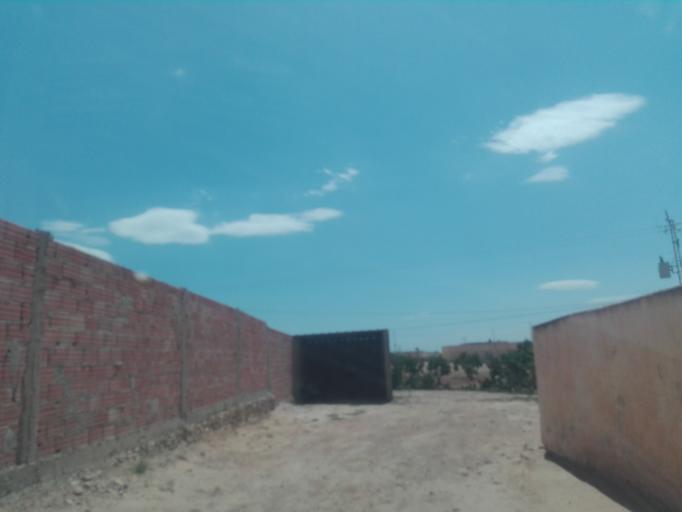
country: TN
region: Safaqis
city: Sfax
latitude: 34.6452
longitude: 10.5891
